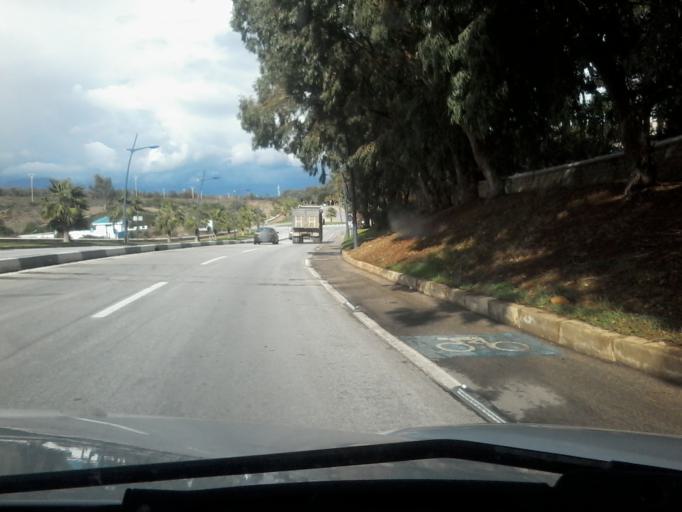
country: ES
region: Ceuta
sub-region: Ceuta
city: Ceuta
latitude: 35.7619
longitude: -5.3487
